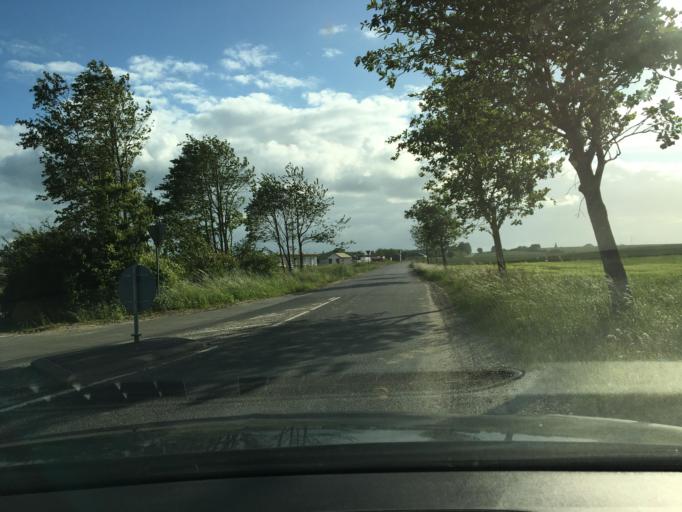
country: DK
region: Central Jutland
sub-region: Favrskov Kommune
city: Hinnerup
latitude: 56.2815
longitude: 10.0714
